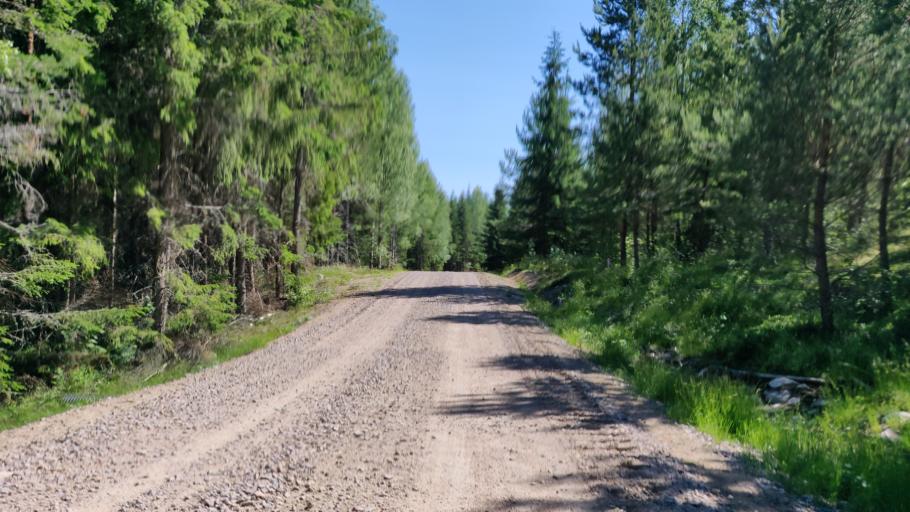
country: SE
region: Vaermland
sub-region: Hagfors Kommun
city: Hagfors
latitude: 59.9869
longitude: 13.5982
